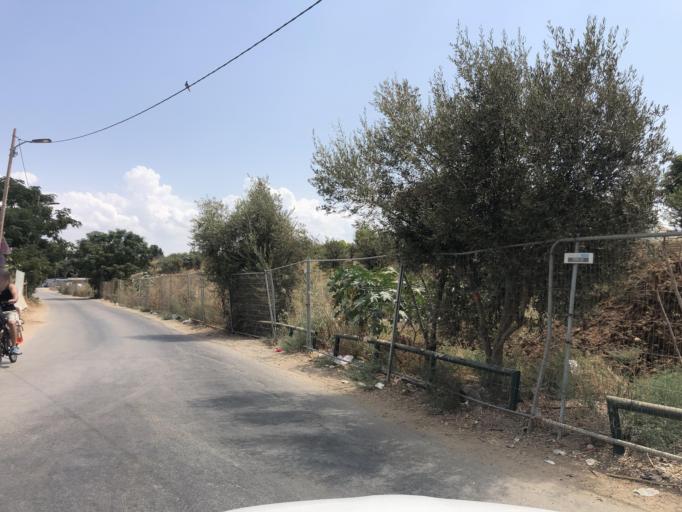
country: IL
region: Tel Aviv
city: Azor
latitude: 32.0428
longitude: 34.7975
